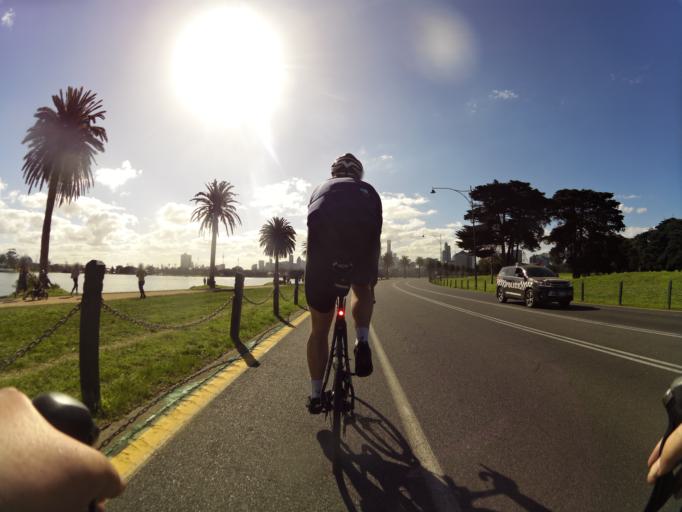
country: AU
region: Victoria
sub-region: Port Phillip
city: Middle Park
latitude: -37.8459
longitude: 144.9708
